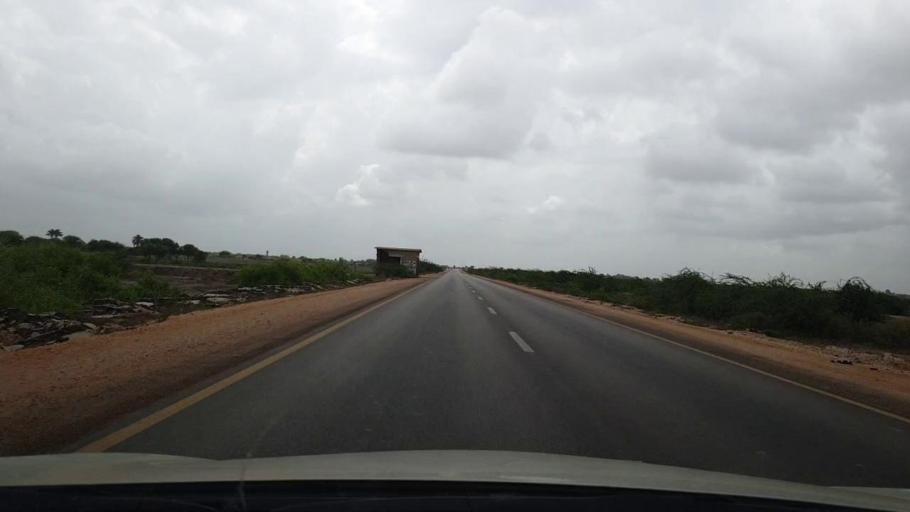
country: PK
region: Sindh
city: Mirpur Batoro
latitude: 24.6350
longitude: 68.3770
